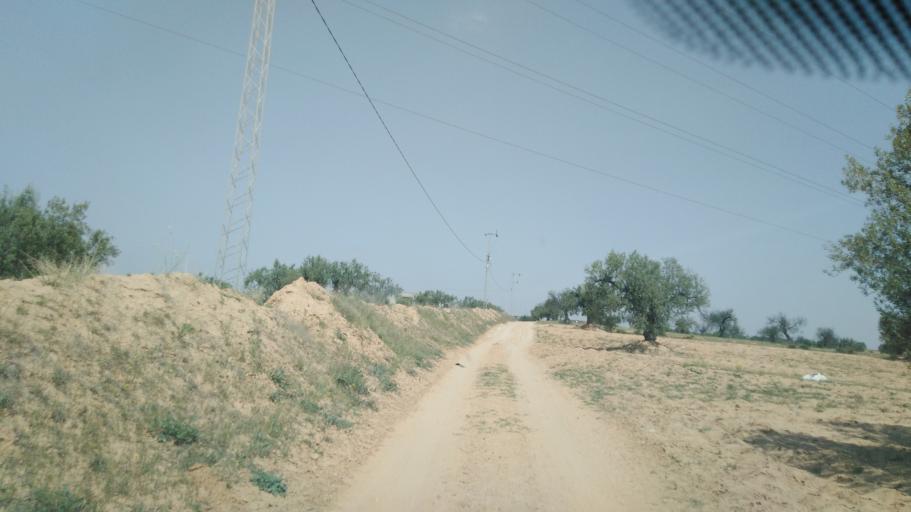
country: TN
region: Safaqis
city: Sfax
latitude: 34.7416
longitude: 10.5712
